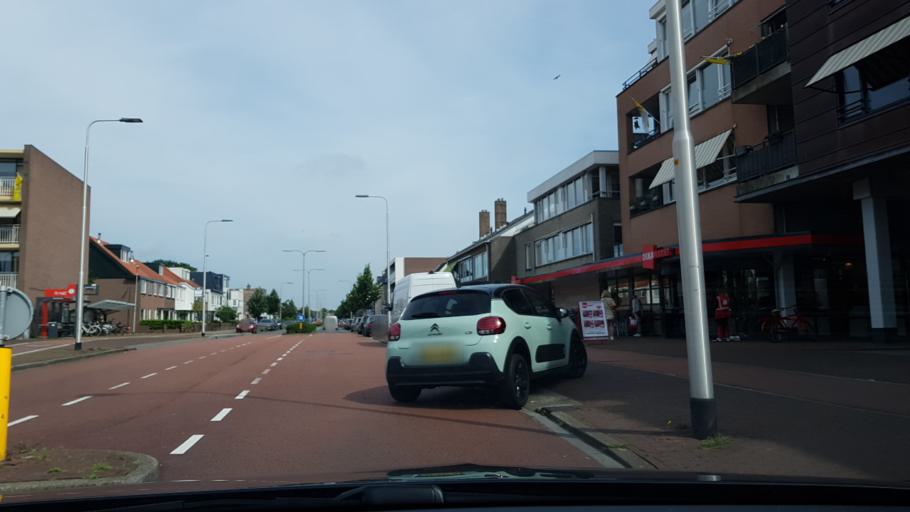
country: NL
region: North Holland
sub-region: Gemeente Velsen
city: Velsen-Zuid
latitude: 52.4333
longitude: 4.6445
